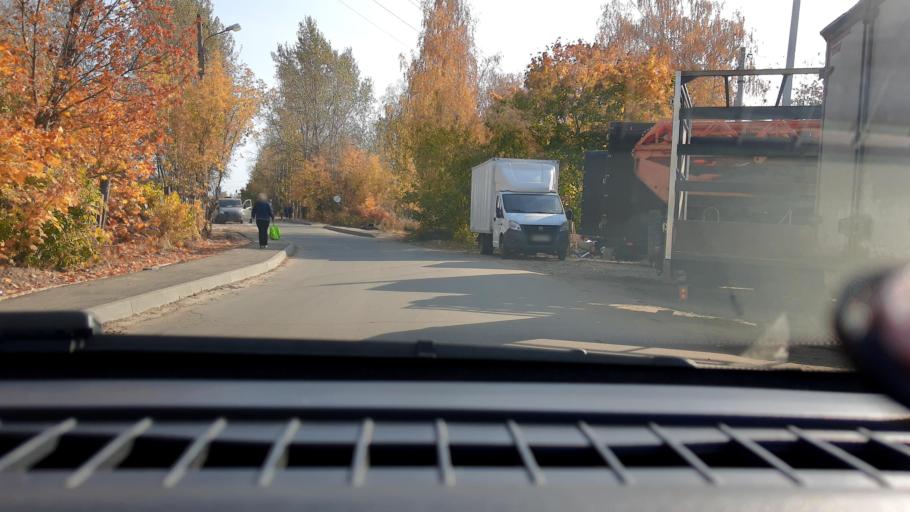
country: RU
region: Nizjnij Novgorod
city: Gorbatovka
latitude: 56.2068
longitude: 43.7656
